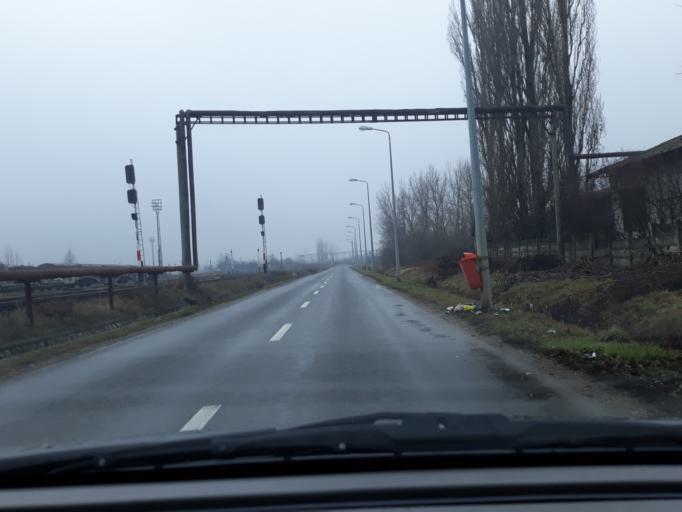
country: RO
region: Bihor
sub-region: Comuna Sanmartin
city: Sanmartin
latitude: 47.0394
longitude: 21.9645
